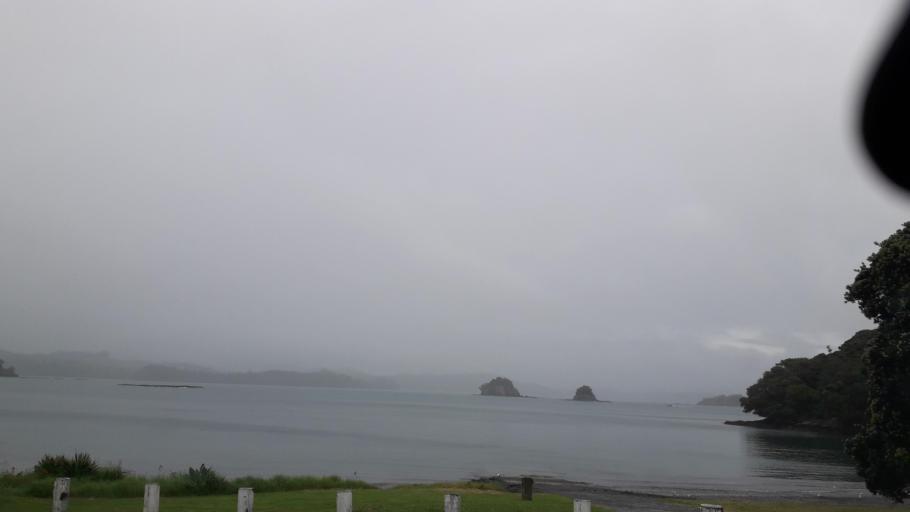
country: NZ
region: Northland
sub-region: Far North District
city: Paihia
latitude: -35.2210
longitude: 174.2562
